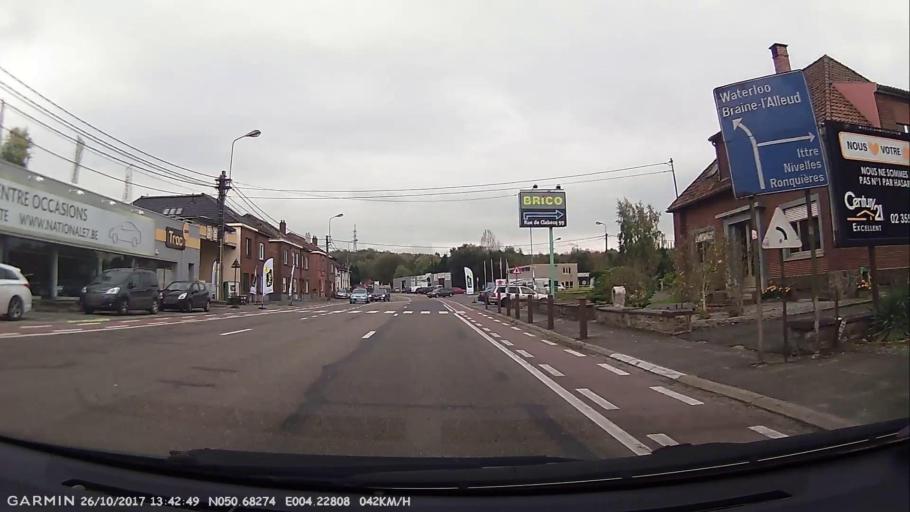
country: BE
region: Wallonia
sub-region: Province du Brabant Wallon
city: Tubize
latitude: 50.6826
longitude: 4.2282
